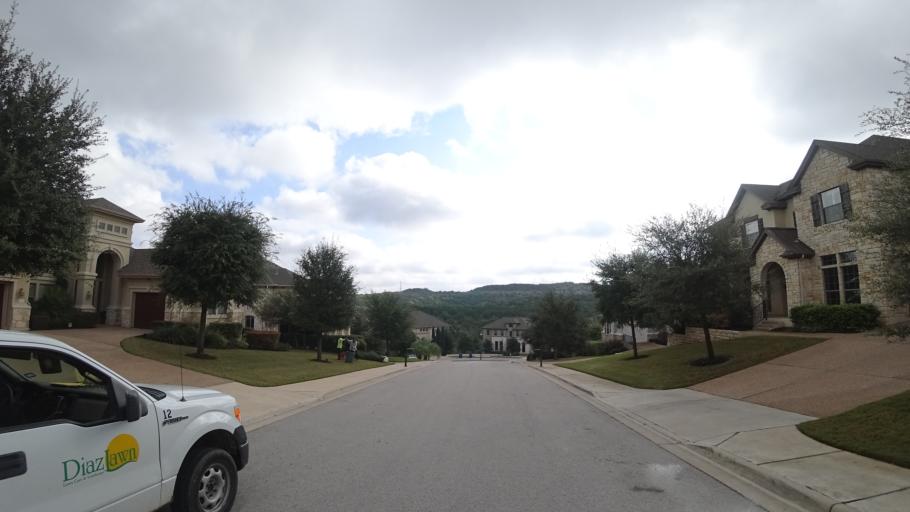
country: US
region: Texas
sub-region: Travis County
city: Barton Creek
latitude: 30.3152
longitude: -97.8958
